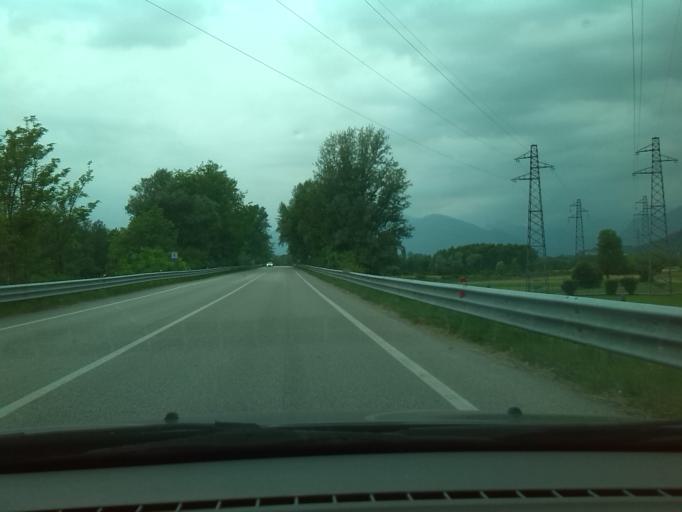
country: IT
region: Friuli Venezia Giulia
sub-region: Provincia di Udine
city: Magnano in Riviera
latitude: 46.2183
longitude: 13.1929
